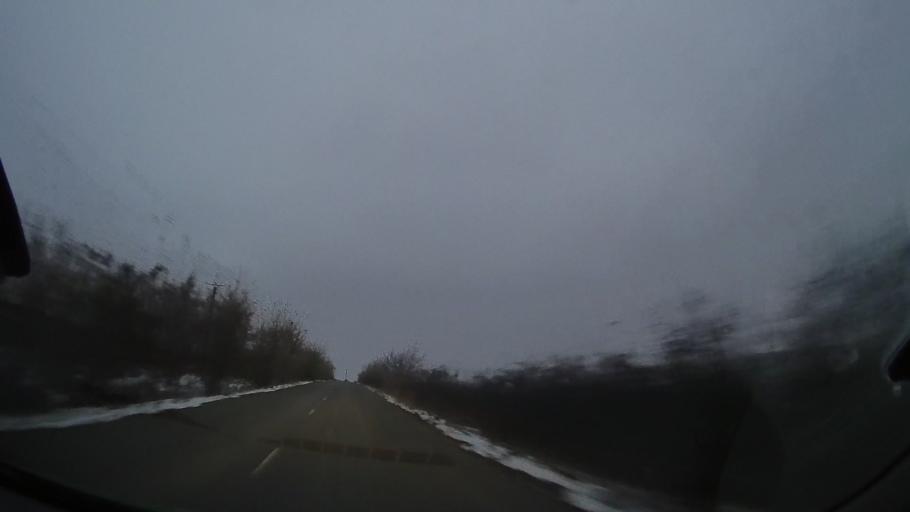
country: RO
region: Vaslui
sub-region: Comuna Gagesti
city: Gagesti
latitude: 46.3971
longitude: 27.9814
